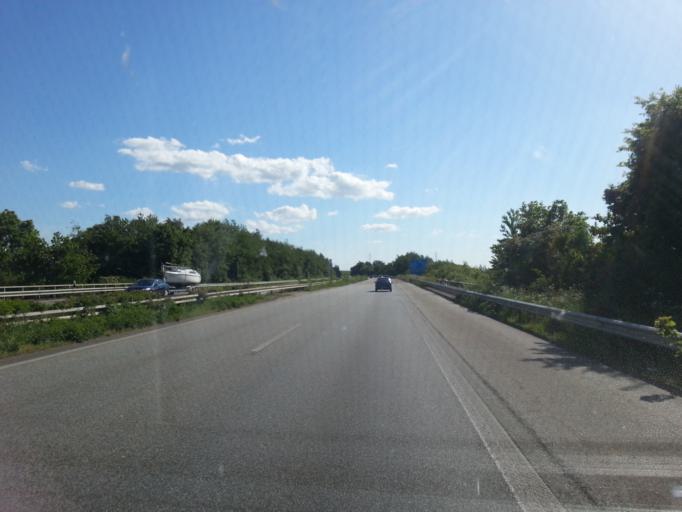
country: DE
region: Schleswig-Holstein
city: Sierksdorf
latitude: 54.0902
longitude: 10.7708
